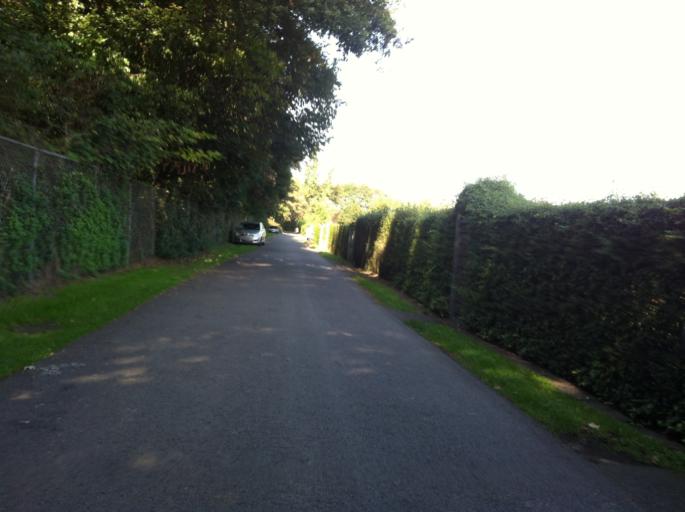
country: DE
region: North Rhine-Westphalia
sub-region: Regierungsbezirk Koln
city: Hoehenberg
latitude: 50.9105
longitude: 7.0235
